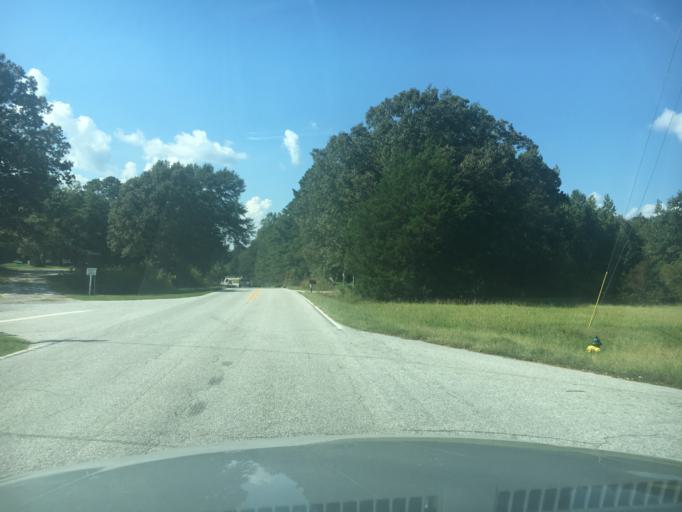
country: US
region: South Carolina
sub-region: Greenwood County
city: Greenwood
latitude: 34.2871
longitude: -82.2052
